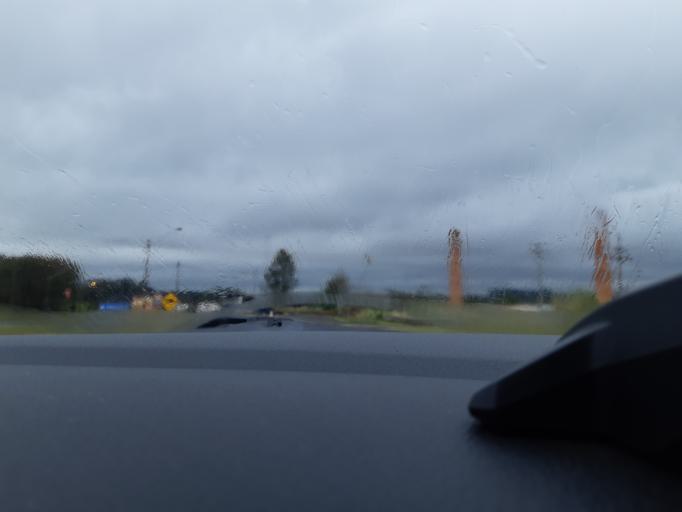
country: BR
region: Sao Paulo
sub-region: Ourinhos
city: Ourinhos
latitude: -23.0023
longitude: -49.9071
